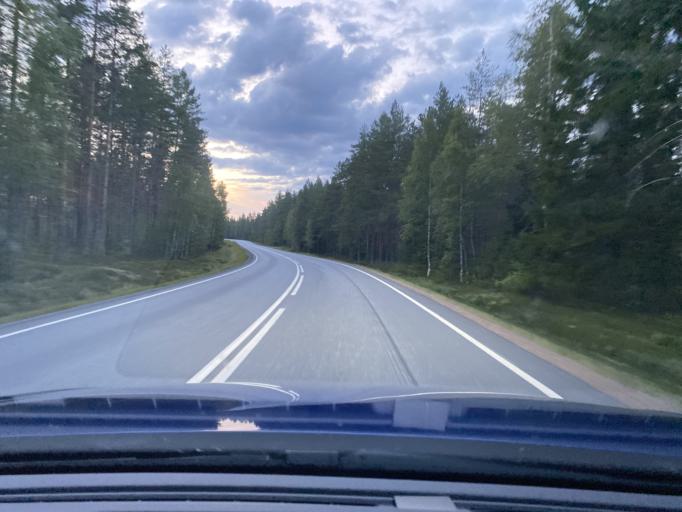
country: FI
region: Southern Ostrobothnia
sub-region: Suupohja
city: Kauhajoki
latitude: 62.2516
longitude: 22.2718
